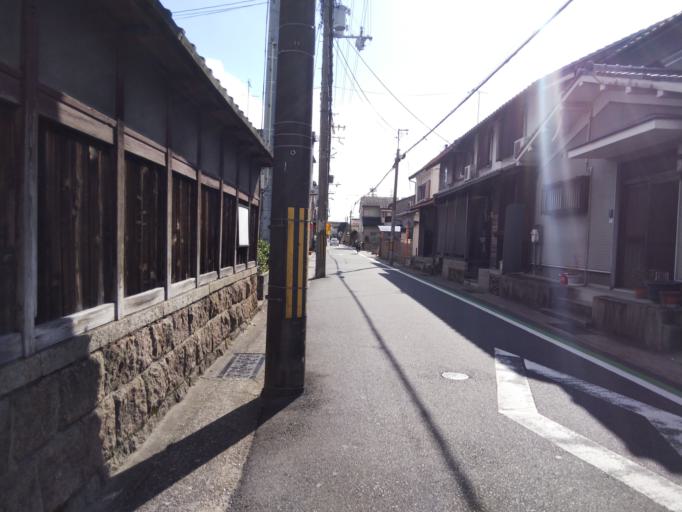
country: JP
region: Kyoto
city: Uji
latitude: 34.9305
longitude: 135.7967
